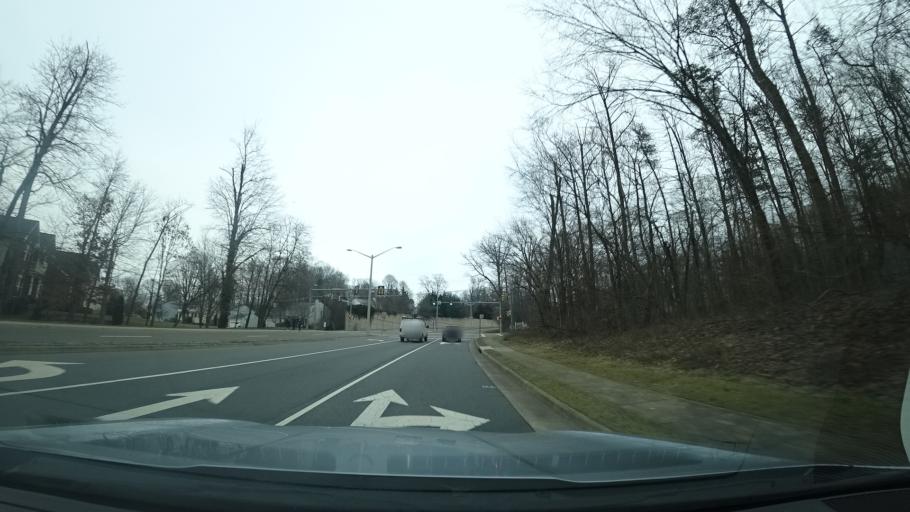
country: US
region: Virginia
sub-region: Fairfax County
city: Herndon
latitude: 38.9827
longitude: -77.3863
